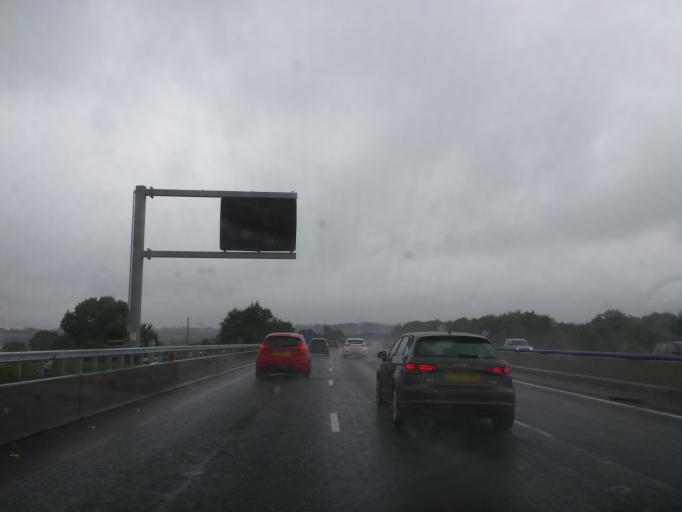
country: GB
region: England
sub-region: Derbyshire
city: Blackwell
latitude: 53.1259
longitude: -1.3301
